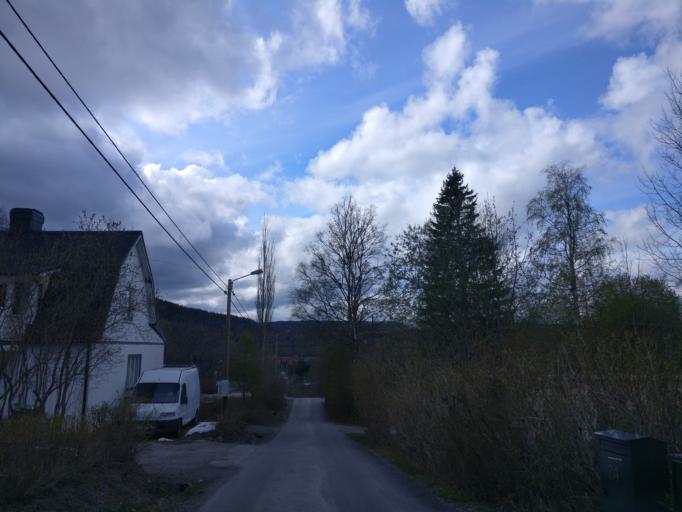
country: SE
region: Vaesternorrland
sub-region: Sundsvalls Kommun
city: Skottsund
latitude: 62.3061
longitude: 17.3943
